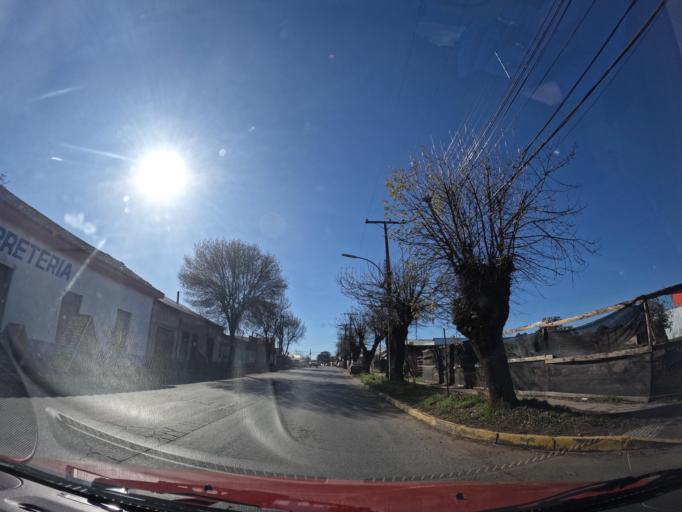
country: CL
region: Maule
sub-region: Provincia de Cauquenes
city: Cauquenes
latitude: -35.9831
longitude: -72.3170
